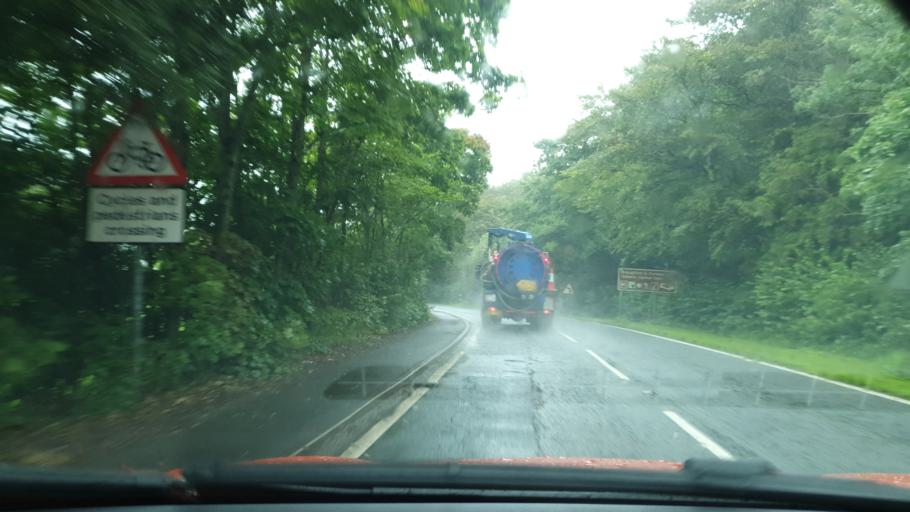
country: GB
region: England
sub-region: Cumbria
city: Millom
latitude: 54.2673
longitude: -3.2154
